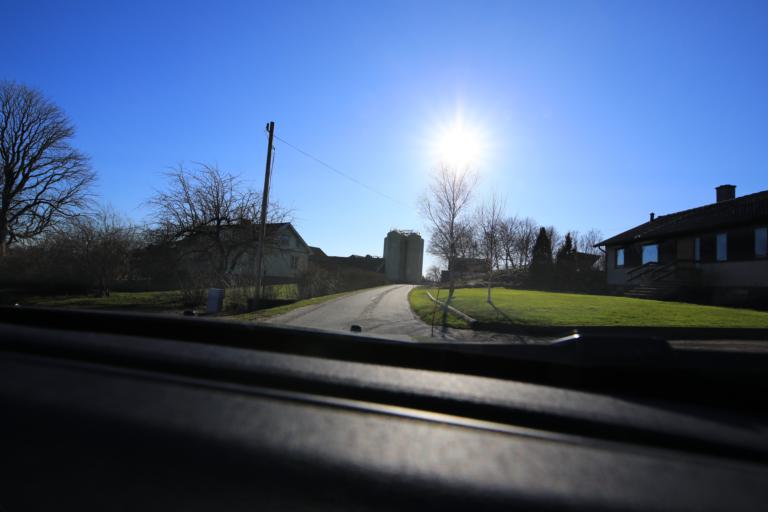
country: SE
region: Halland
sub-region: Varbergs Kommun
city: Tvaaker
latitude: 57.0584
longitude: 12.3728
